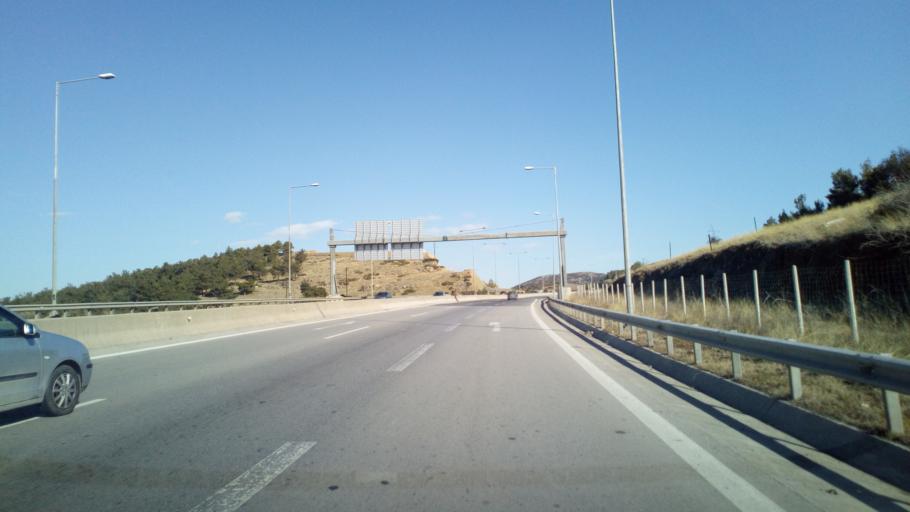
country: GR
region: Central Macedonia
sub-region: Nomos Thessalonikis
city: Efkarpia
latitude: 40.6851
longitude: 22.9579
